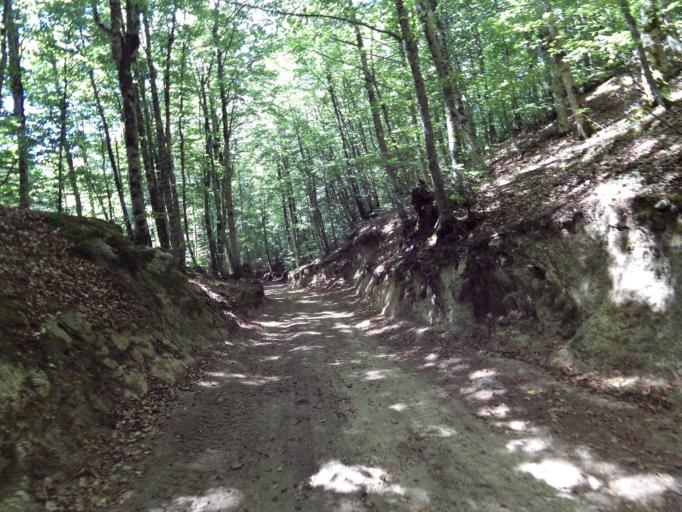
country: IT
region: Calabria
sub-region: Provincia di Vibo-Valentia
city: Mongiana
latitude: 38.5193
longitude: 16.3452
